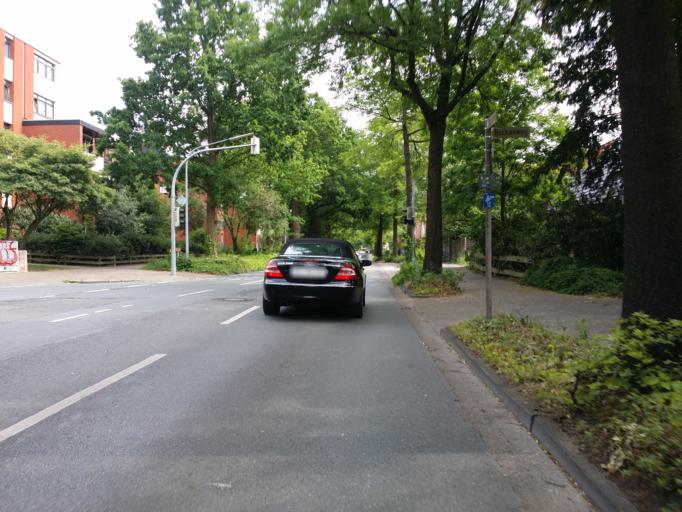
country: DE
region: Lower Saxony
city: Oldenburg
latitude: 53.1672
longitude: 8.2141
